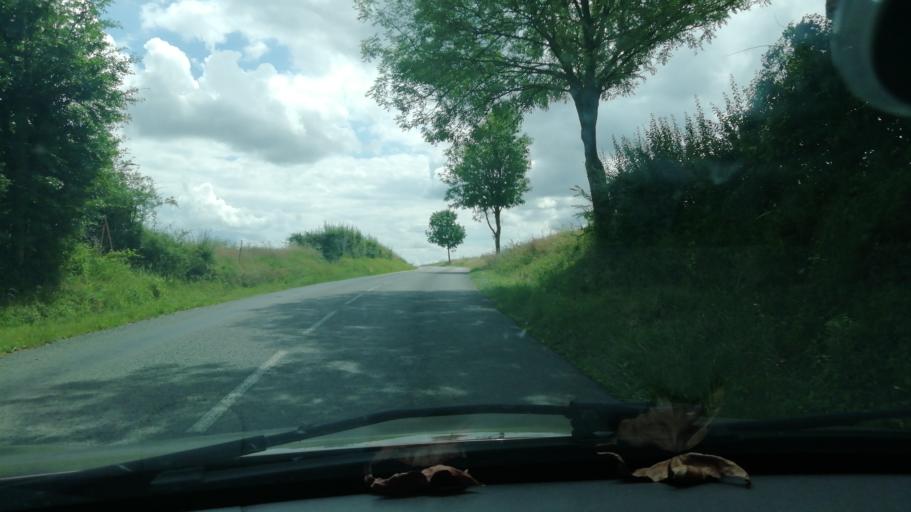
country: FR
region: Nord-Pas-de-Calais
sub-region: Departement du Pas-de-Calais
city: Aubigny-en-Artois
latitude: 50.3376
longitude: 2.5891
